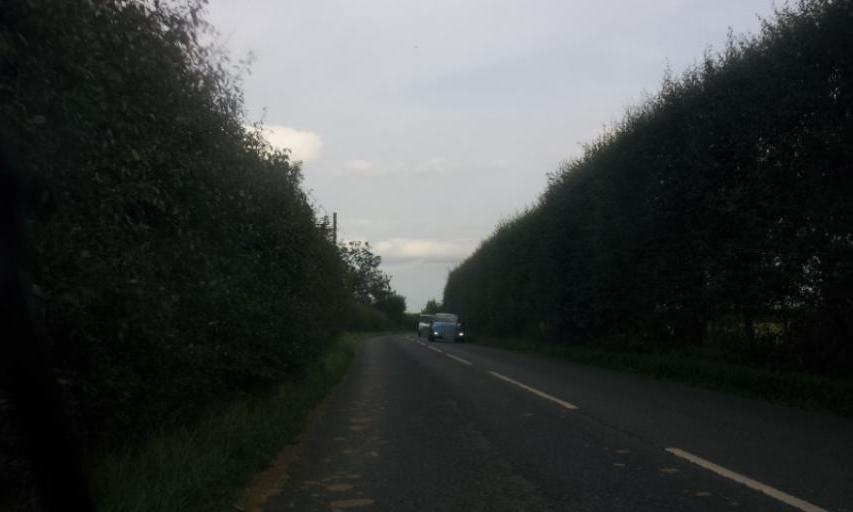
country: GB
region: England
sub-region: Kent
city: Hadlow
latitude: 51.2121
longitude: 0.3189
